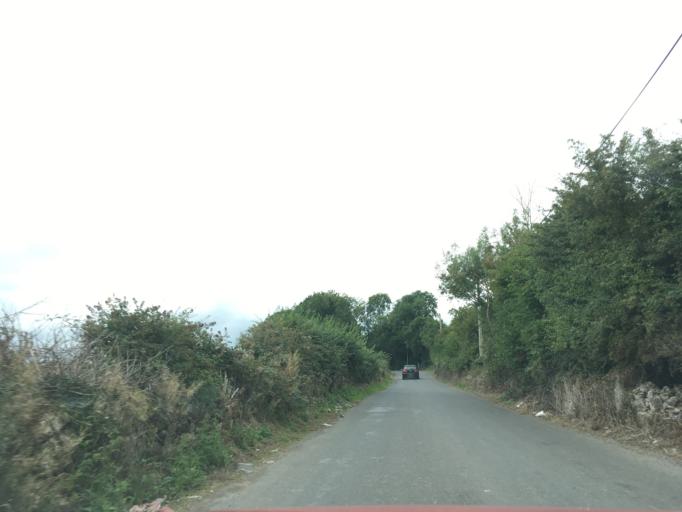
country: IE
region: Munster
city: Cahir
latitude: 52.4602
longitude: -8.0025
